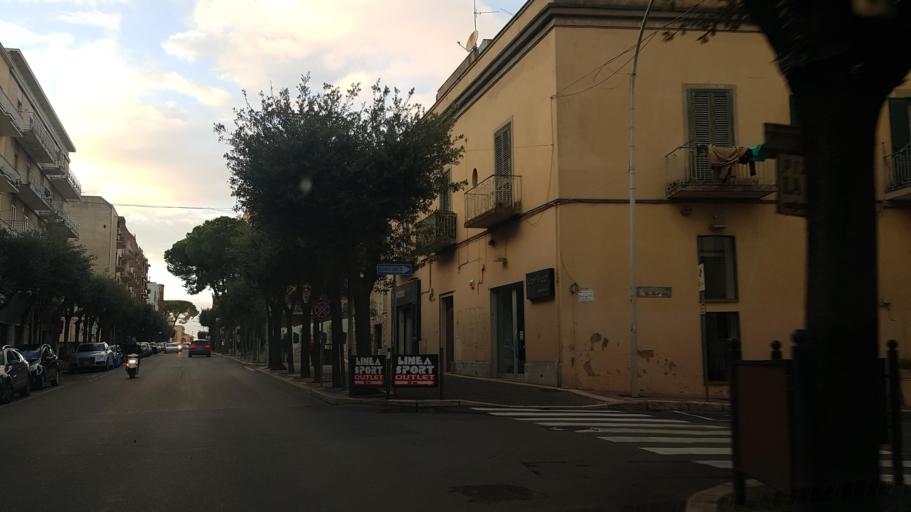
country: IT
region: Basilicate
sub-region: Provincia di Matera
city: Matera
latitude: 40.6716
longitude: 16.6046
